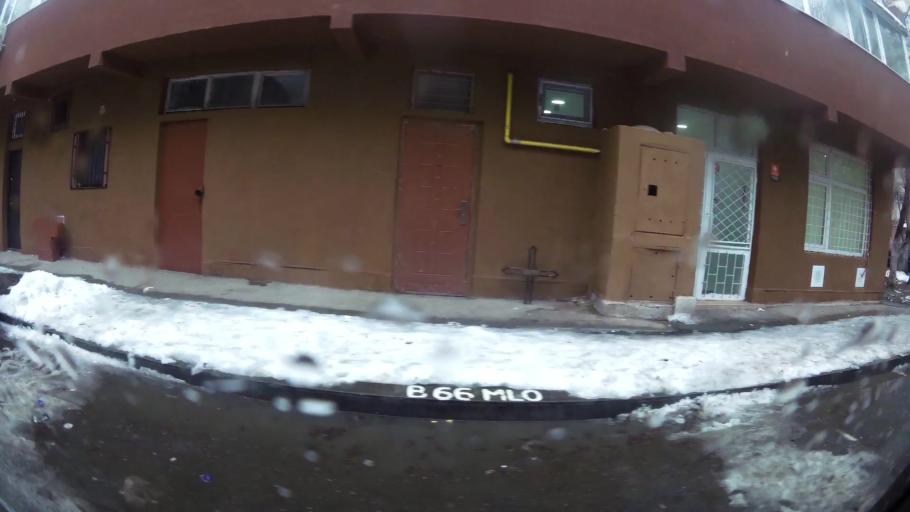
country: RO
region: Ilfov
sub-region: Comuna Chiajna
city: Rosu
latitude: 44.4128
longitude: 26.0207
